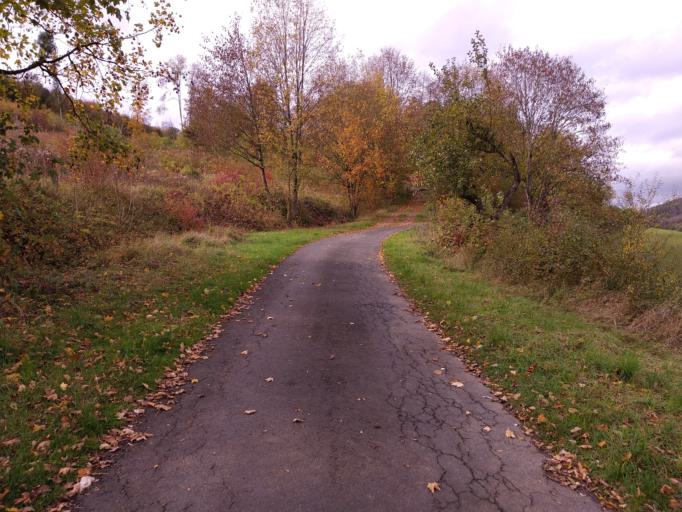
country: DE
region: North Rhine-Westphalia
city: Beverungen
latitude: 51.6710
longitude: 9.3600
